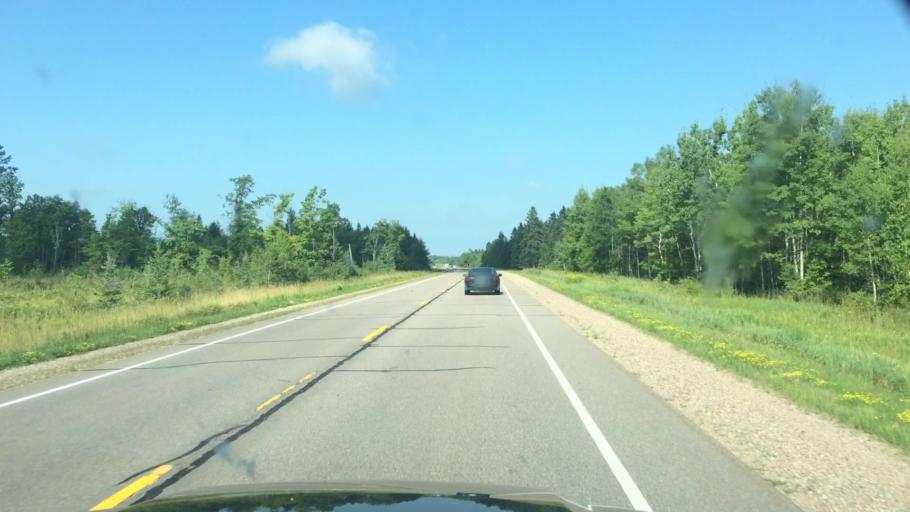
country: US
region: Wisconsin
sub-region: Langlade County
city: Antigo
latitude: 45.1456
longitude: -89.3206
